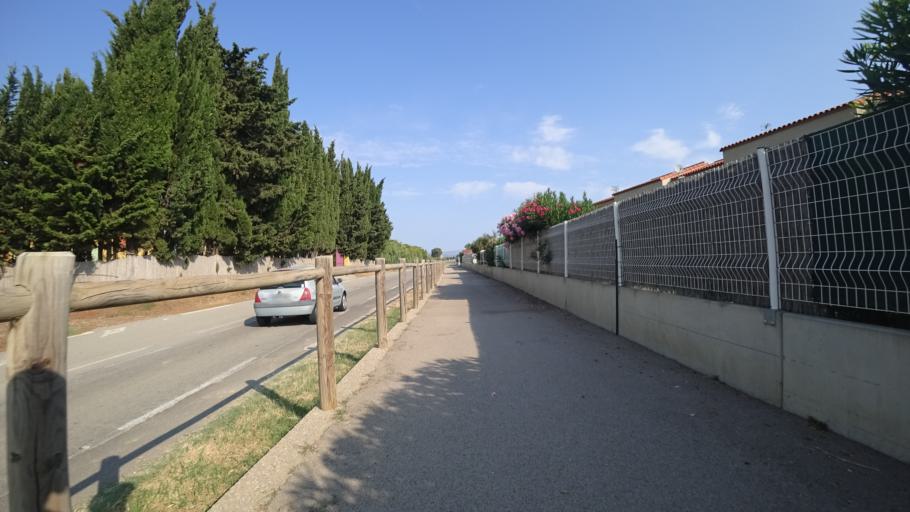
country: FR
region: Languedoc-Roussillon
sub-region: Departement des Pyrenees-Orientales
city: Saint-Laurent-de-la-Salanque
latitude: 42.7671
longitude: 2.9811
